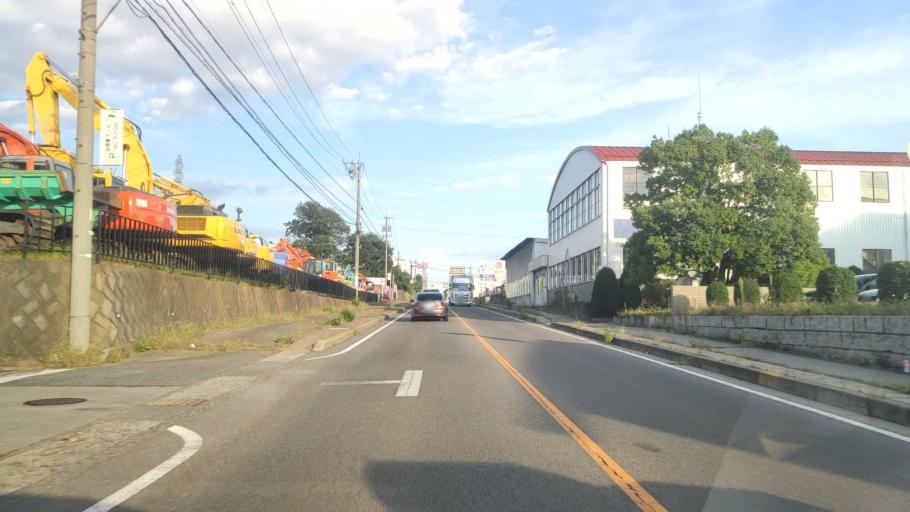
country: JP
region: Nagano
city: Komoro
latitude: 36.3514
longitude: 138.3553
